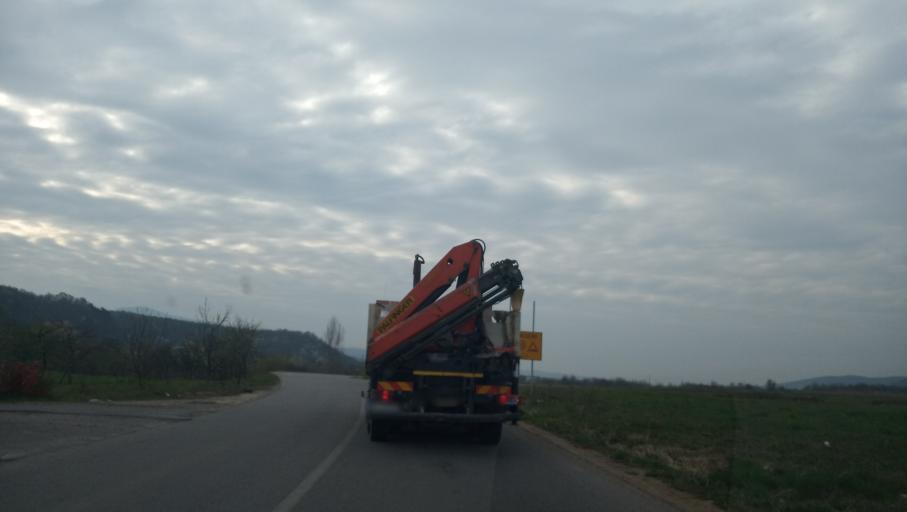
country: RO
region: Bihor
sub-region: Comuna Lunca
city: Lunca
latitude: 46.5173
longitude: 22.4662
